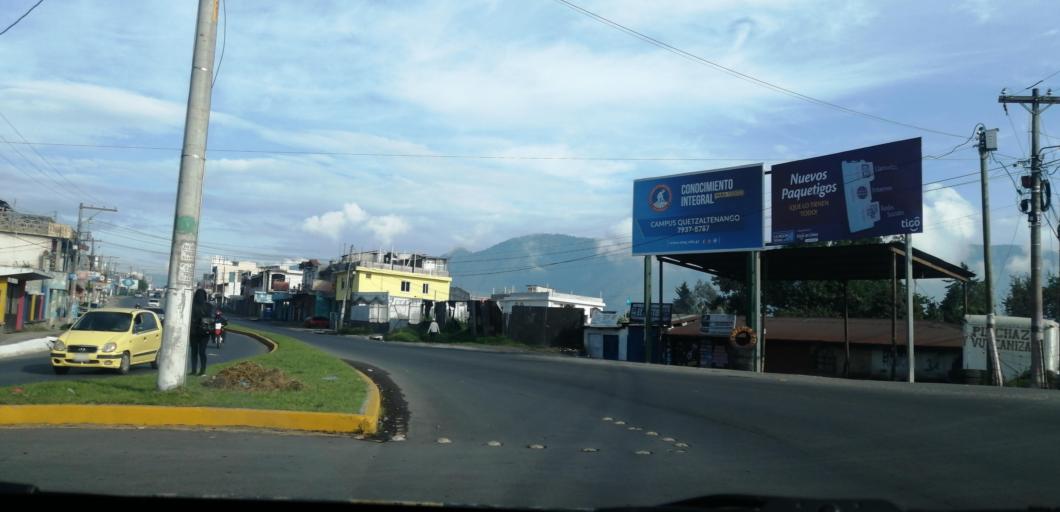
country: GT
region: Quetzaltenango
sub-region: Municipio de La Esperanza
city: La Esperanza
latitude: 14.8626
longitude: -91.5543
